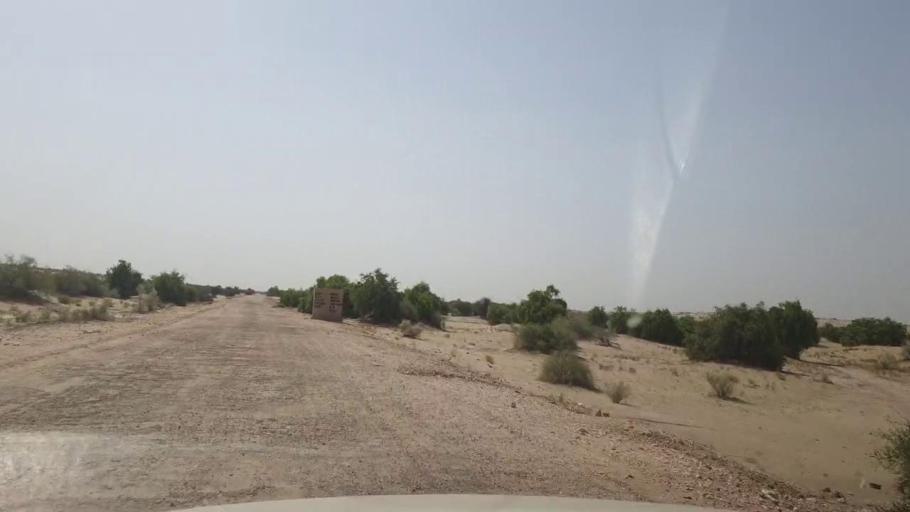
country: PK
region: Sindh
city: Rohri
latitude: 27.4544
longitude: 69.2245
